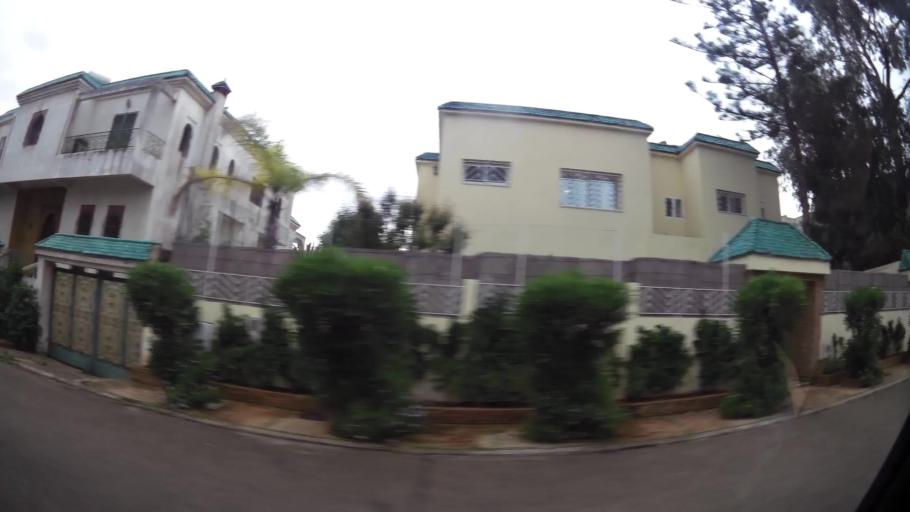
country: MA
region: Grand Casablanca
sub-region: Casablanca
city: Casablanca
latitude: 33.5776
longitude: -7.6778
